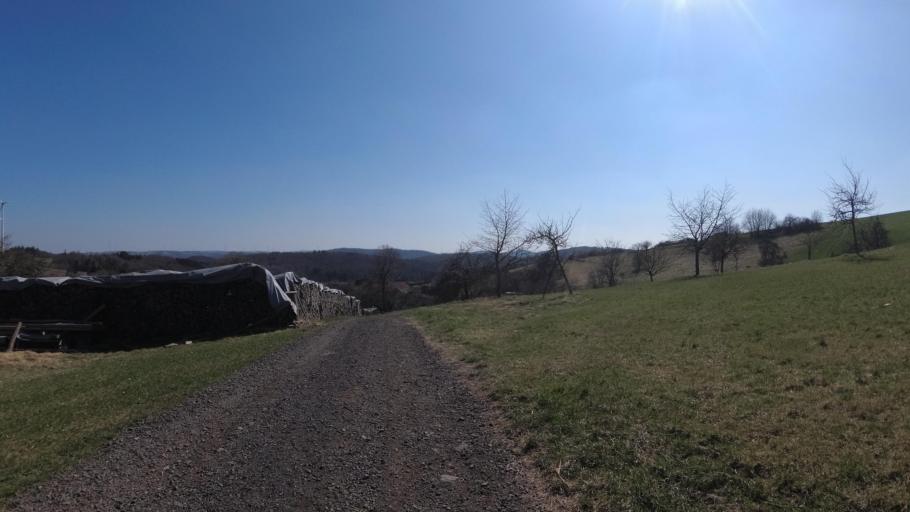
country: DE
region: Rheinland-Pfalz
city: Dambach
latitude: 49.6291
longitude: 7.1301
